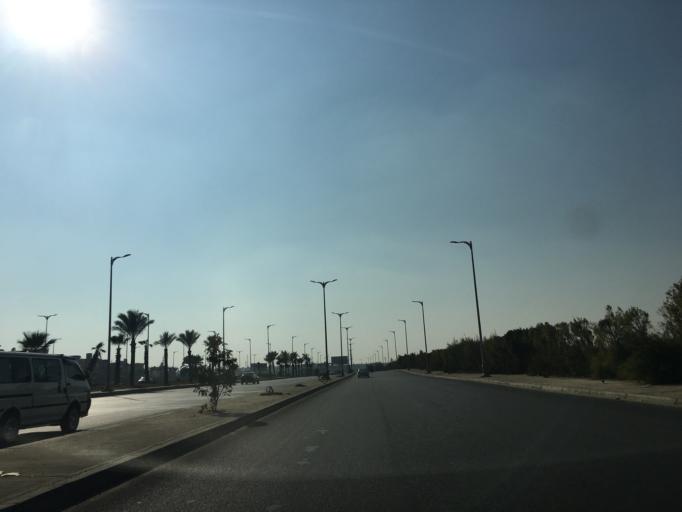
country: EG
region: Al Jizah
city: Madinat Sittah Uktubar
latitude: 29.9925
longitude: 30.9563
